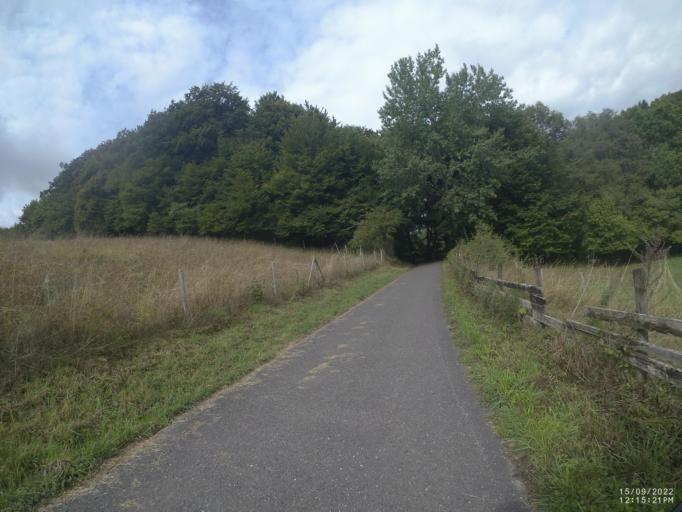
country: DE
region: Rheinland-Pfalz
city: Oberehe-Stroheich
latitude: 50.3121
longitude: 6.7489
